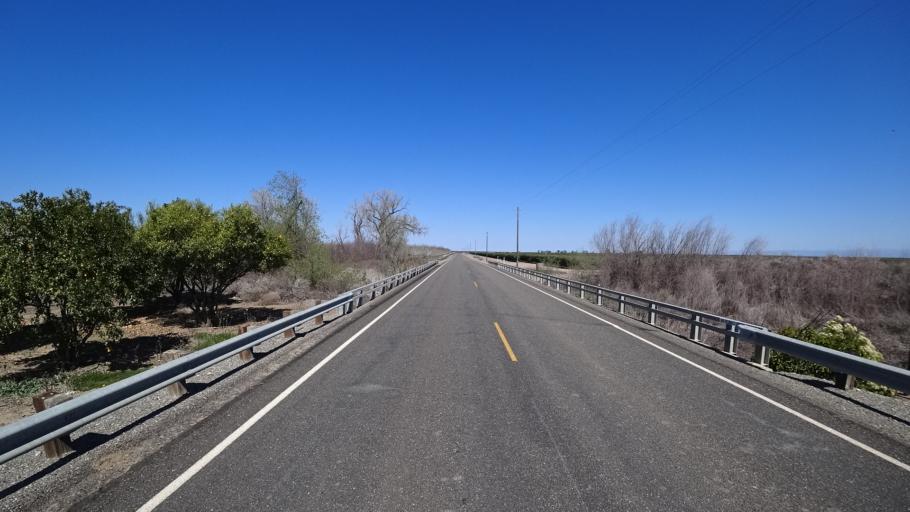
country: US
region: California
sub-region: Glenn County
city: Willows
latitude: 39.6171
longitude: -122.2500
